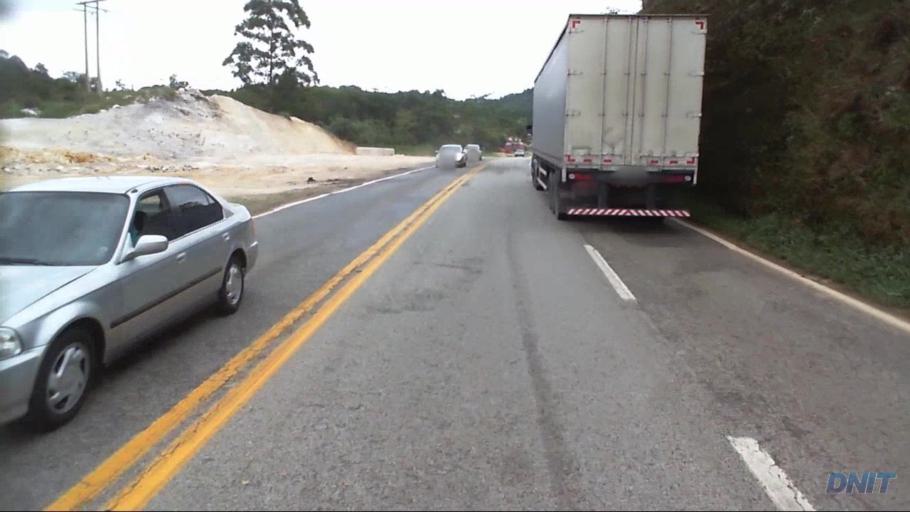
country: BR
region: Minas Gerais
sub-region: Caete
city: Caete
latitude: -19.7519
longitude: -43.5254
